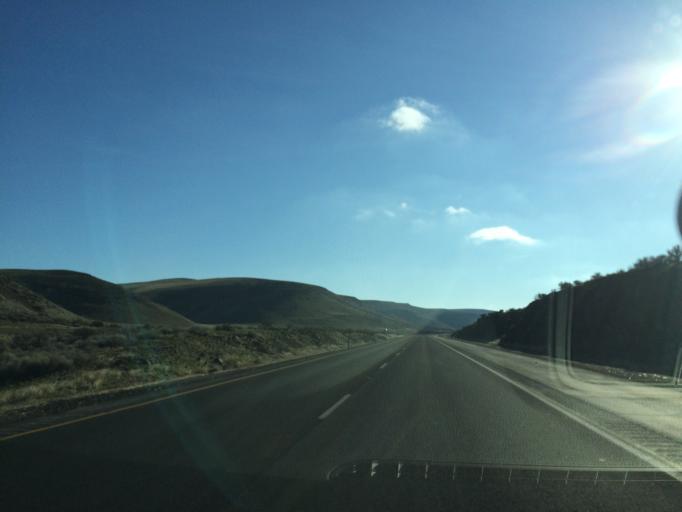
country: US
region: Washington
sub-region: Grant County
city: Quincy
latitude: 46.9959
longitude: -119.9735
